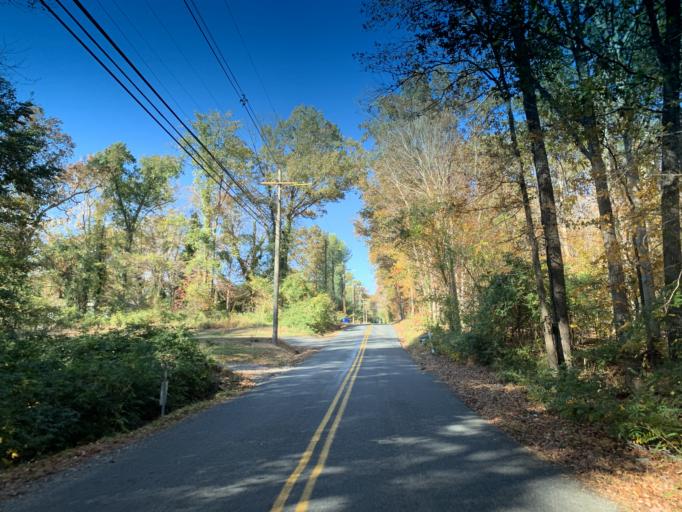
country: US
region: Maryland
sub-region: Harford County
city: Joppatowne
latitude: 39.4511
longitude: -76.3382
